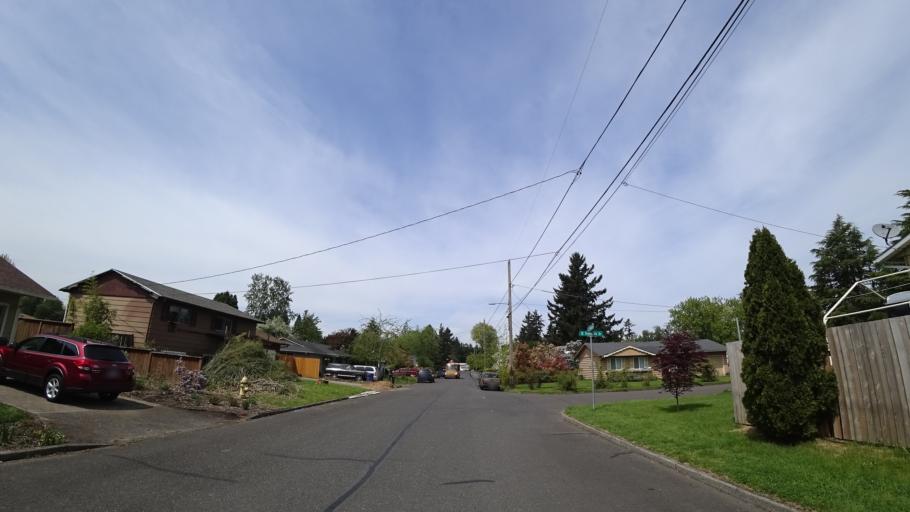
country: US
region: Oregon
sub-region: Clackamas County
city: Milwaukie
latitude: 45.4564
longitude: -122.6091
